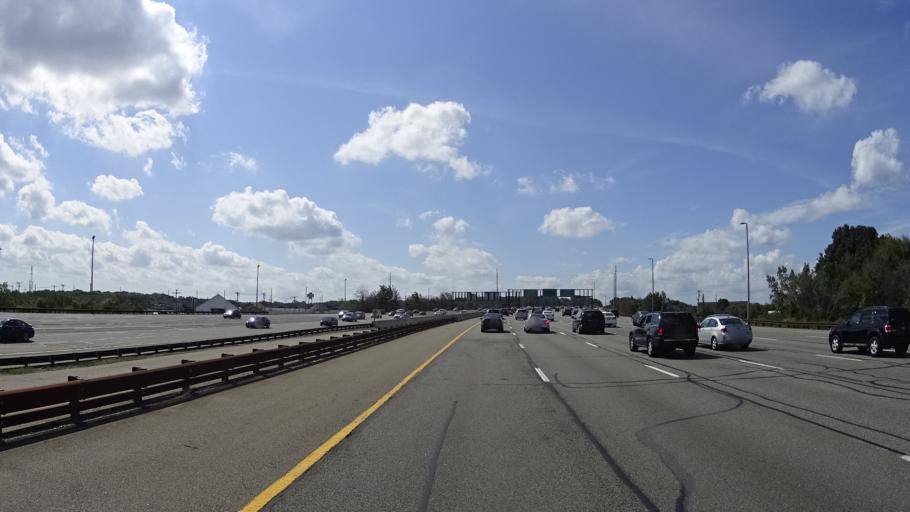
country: US
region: New Jersey
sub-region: Middlesex County
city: South Amboy
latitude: 40.4968
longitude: -74.3007
